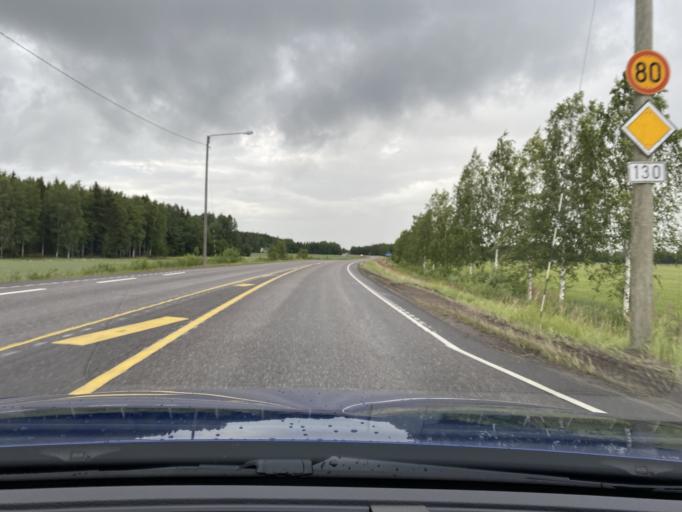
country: FI
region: Uusimaa
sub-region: Helsinki
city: Hyvinge
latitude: 60.5788
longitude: 24.7965
